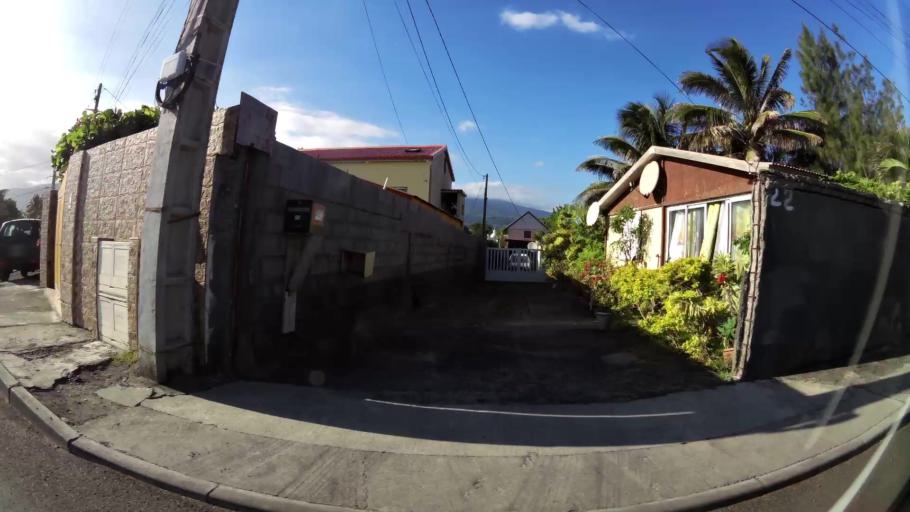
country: RE
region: Reunion
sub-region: Reunion
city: Saint-Louis
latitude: -21.2951
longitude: 55.3968
